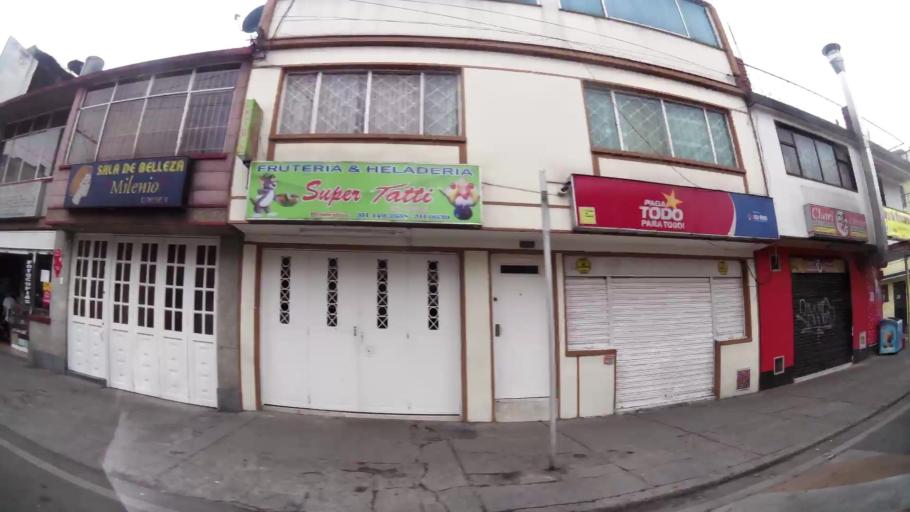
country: CO
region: Bogota D.C.
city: Bogota
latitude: 4.6719
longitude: -74.0988
